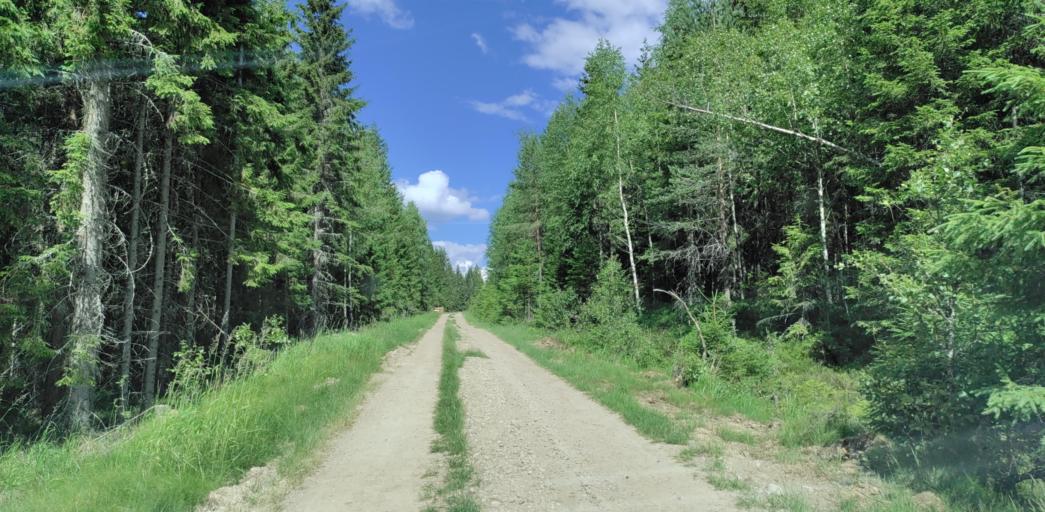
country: SE
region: Vaermland
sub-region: Hagfors Kommun
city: Ekshaerad
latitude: 60.0656
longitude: 13.3404
